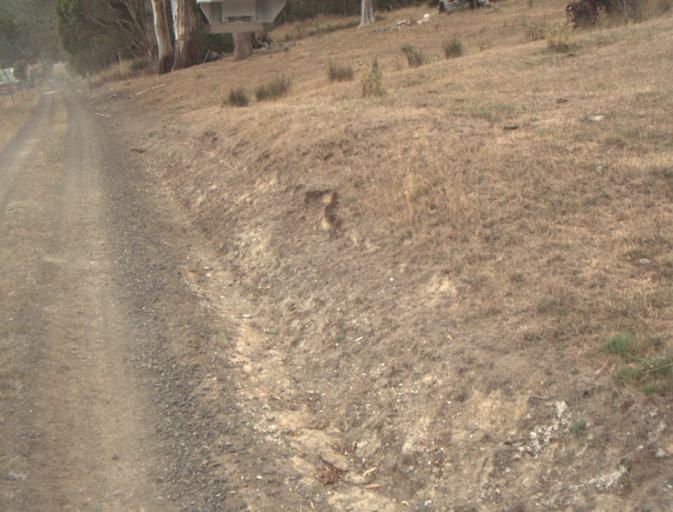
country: AU
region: Tasmania
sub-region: Launceston
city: Mayfield
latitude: -41.2406
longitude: 147.1859
